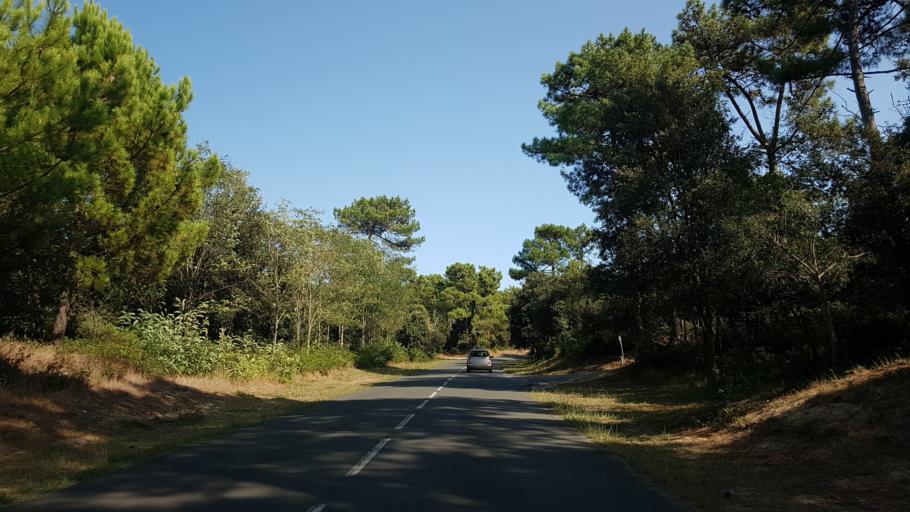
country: FR
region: Poitou-Charentes
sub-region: Departement de la Charente-Maritime
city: Les Mathes
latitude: 45.6993
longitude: -1.2242
